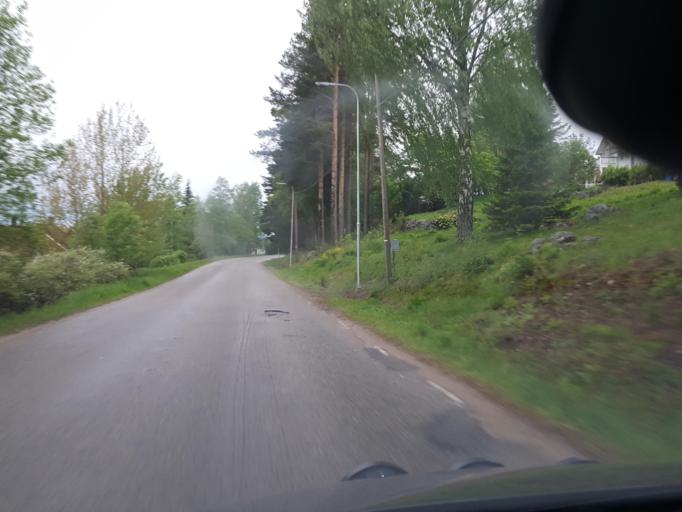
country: SE
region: Gaevleborg
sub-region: Ljusdals Kommun
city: Ljusdal
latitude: 61.8195
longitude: 16.1310
